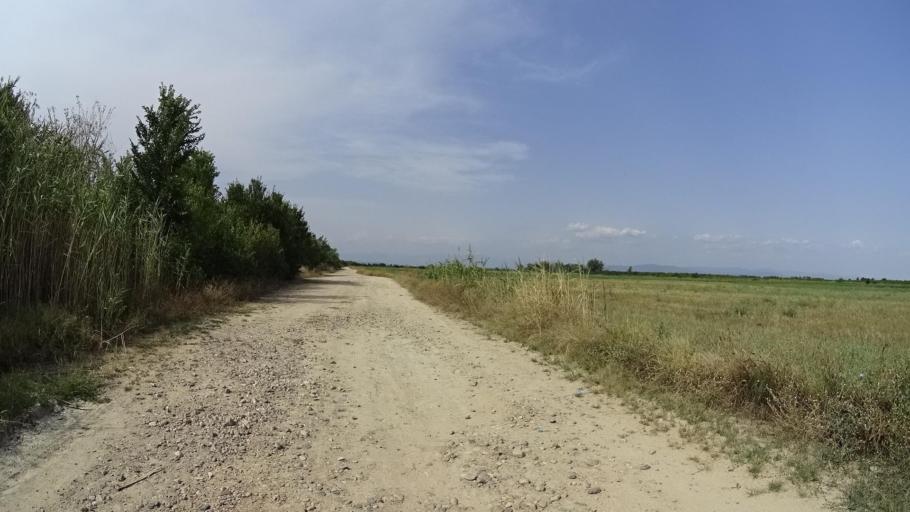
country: BG
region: Plovdiv
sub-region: Obshtina Kaloyanovo
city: Kaloyanovo
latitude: 42.2911
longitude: 24.7962
